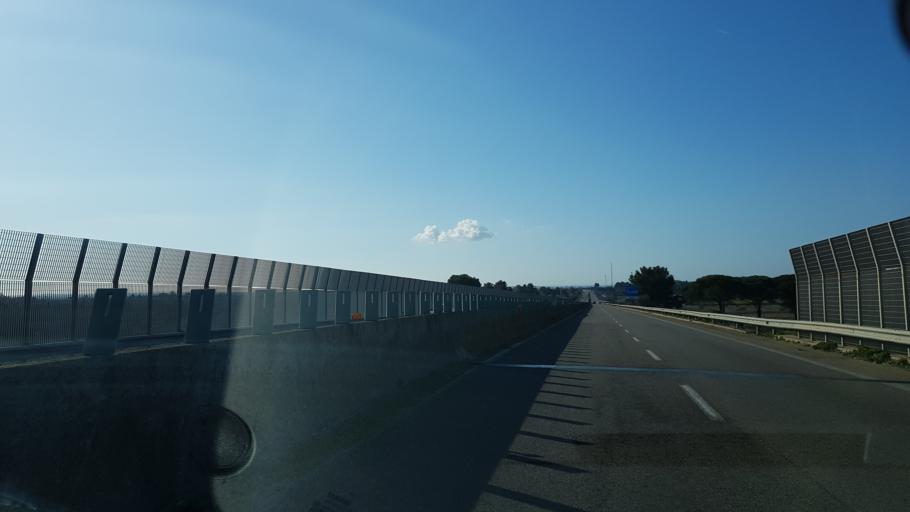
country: IT
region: Apulia
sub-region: Provincia di Lecce
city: Sannicola
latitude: 40.1120
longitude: 18.0405
